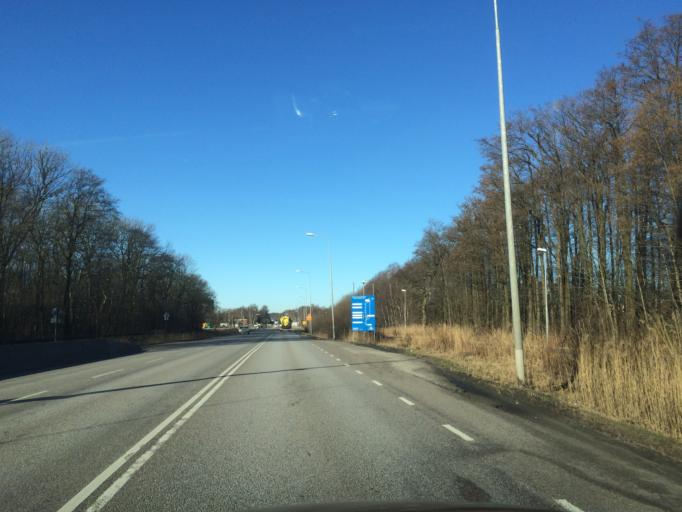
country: SE
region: Vaestra Goetaland
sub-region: Goteborg
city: Majorna
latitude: 57.6985
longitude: 11.8877
